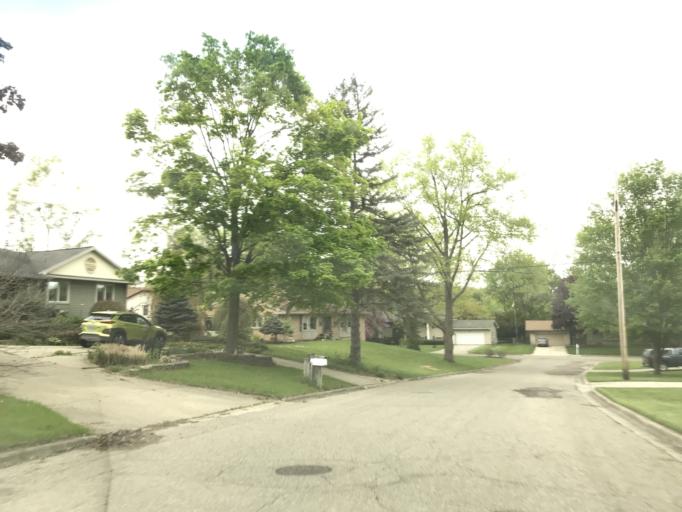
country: US
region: Michigan
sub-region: Eaton County
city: Waverly
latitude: 42.7572
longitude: -84.6167
